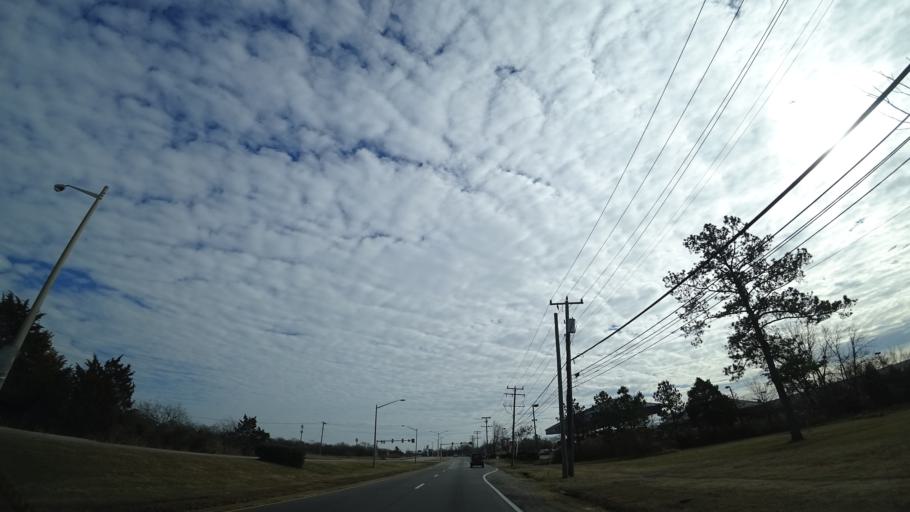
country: US
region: Virginia
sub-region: City of Hampton
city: Hampton
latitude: 37.0368
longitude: -76.3683
